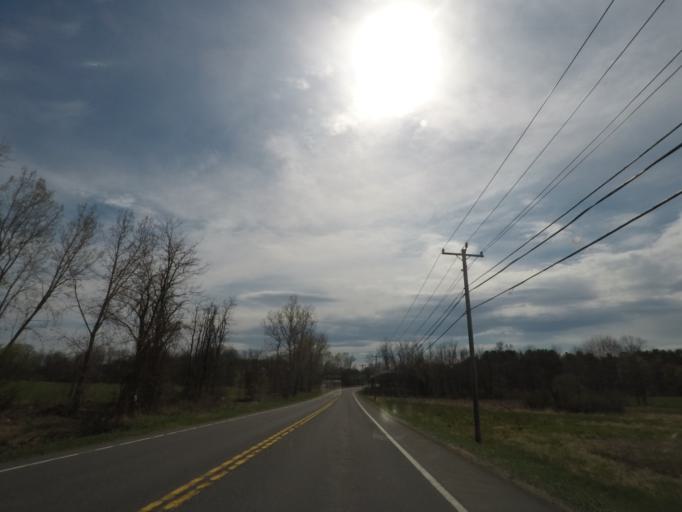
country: US
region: New York
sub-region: Columbia County
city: Chatham
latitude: 42.3147
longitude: -73.6346
